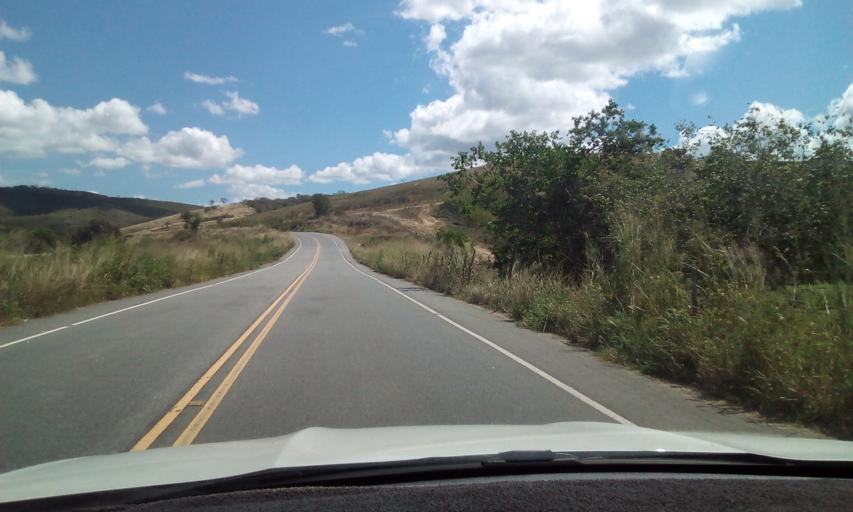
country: BR
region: Paraiba
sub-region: Serra Redonda
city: Alagoa Grande
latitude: -7.1584
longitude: -35.6018
